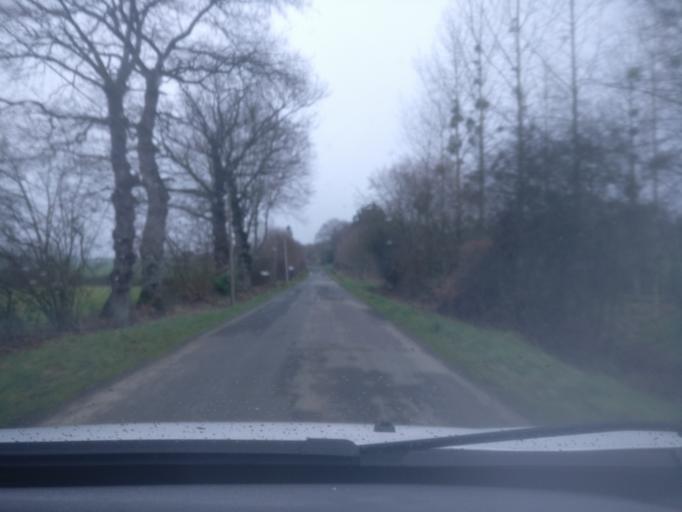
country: FR
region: Brittany
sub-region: Departement d'Ille-et-Vilaine
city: Saint-Medard-sur-Ille
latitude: 48.2948
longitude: -1.6077
